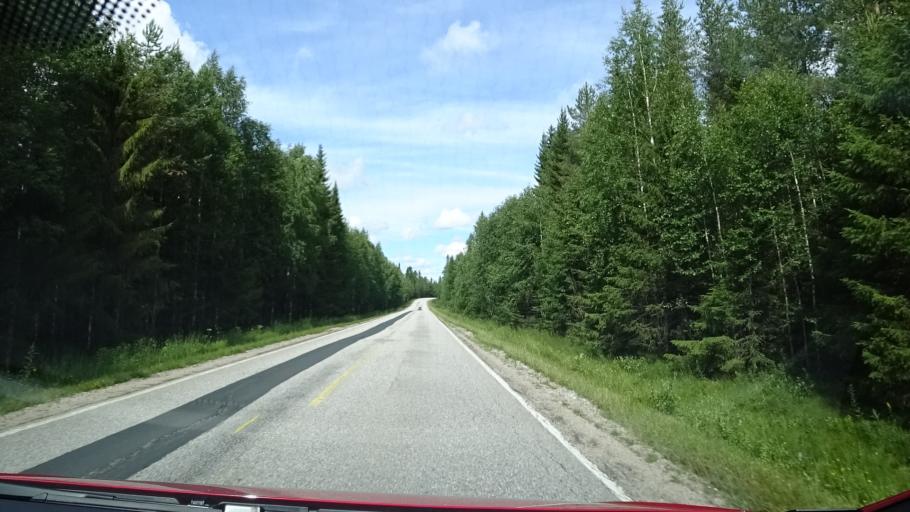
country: FI
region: Kainuu
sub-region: Kehys-Kainuu
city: Kuhmo
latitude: 64.4519
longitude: 29.7791
